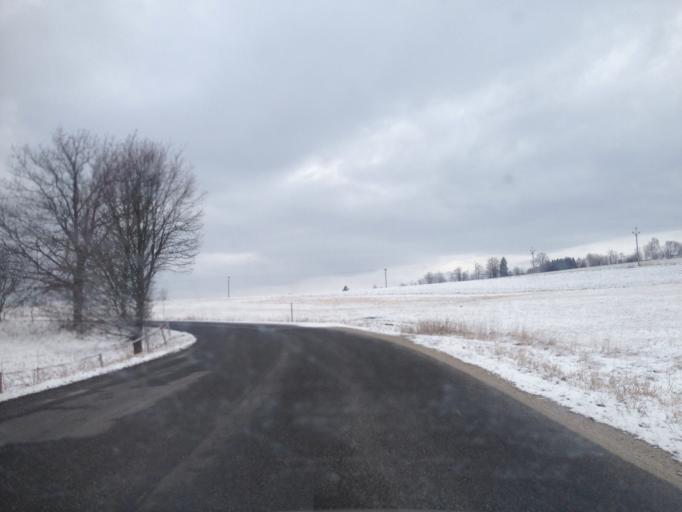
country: CZ
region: Liberecky
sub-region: Okres Semily
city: Ponikla
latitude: 50.6478
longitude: 15.4267
